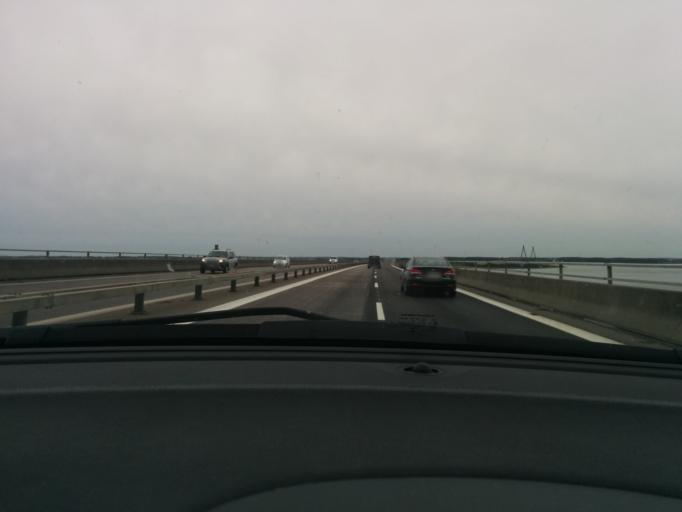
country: DK
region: Zealand
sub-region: Vordingborg Kommune
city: Nyrad
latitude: 54.9695
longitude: 12.0023
